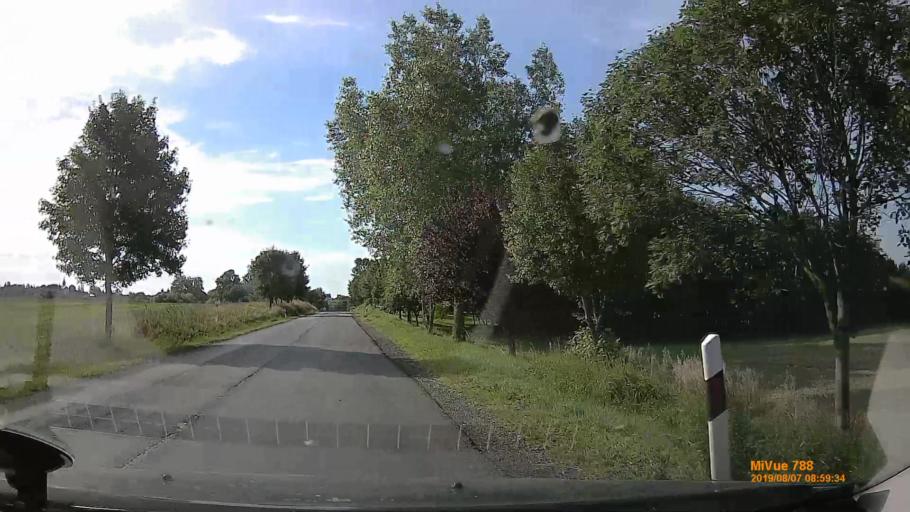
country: HU
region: Zala
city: Pacsa
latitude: 46.7337
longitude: 16.9392
